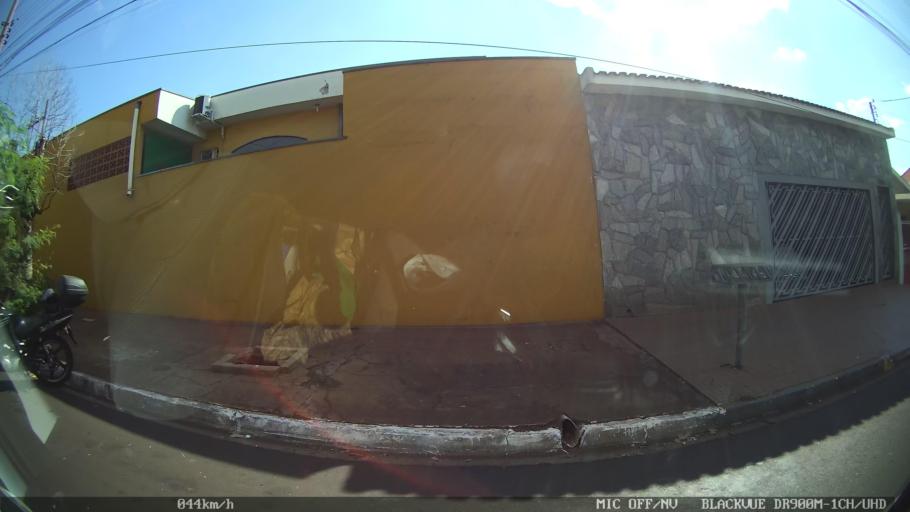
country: BR
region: Sao Paulo
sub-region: Ribeirao Preto
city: Ribeirao Preto
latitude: -21.1833
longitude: -47.8332
